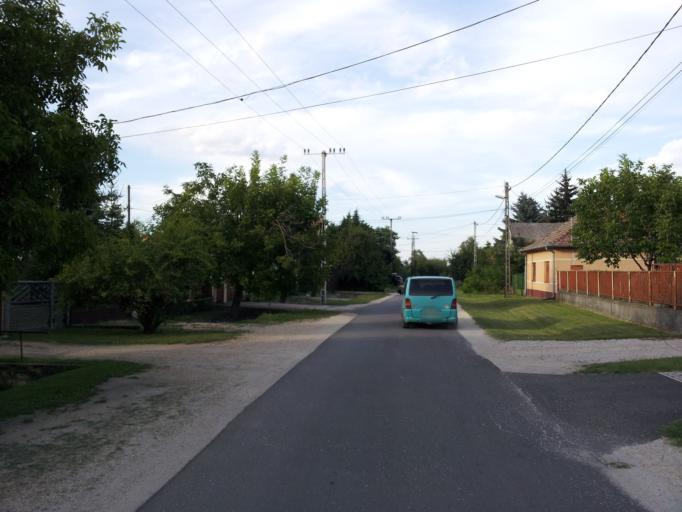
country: HU
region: Pest
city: Kiskunlachaza
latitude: 47.1925
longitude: 19.0128
